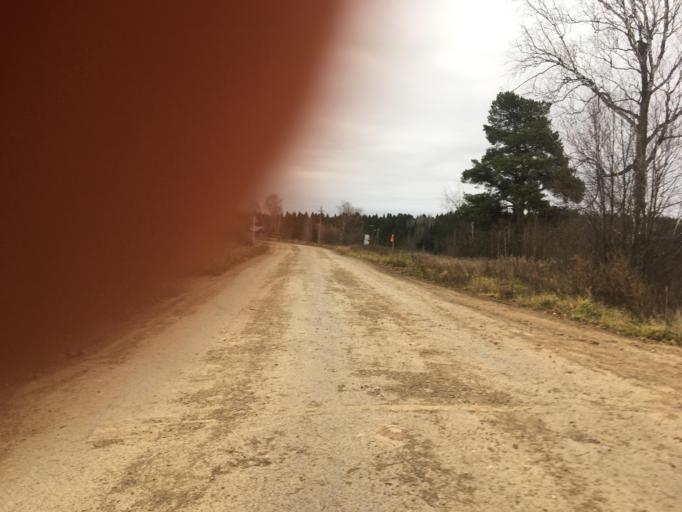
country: RU
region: Perm
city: Komarikhinskiy
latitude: 58.0881
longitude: 57.1113
